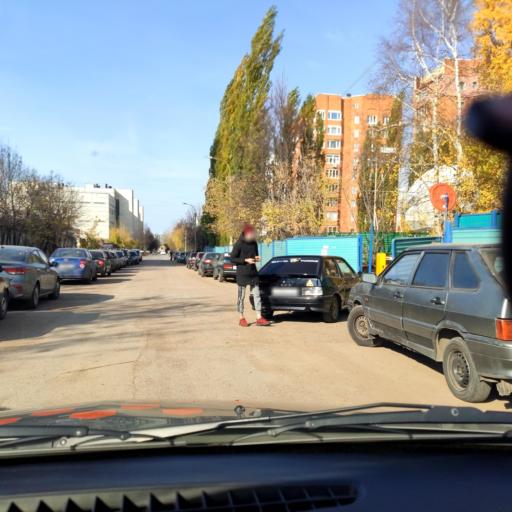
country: RU
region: Bashkortostan
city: Ufa
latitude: 54.7153
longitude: 56.0140
